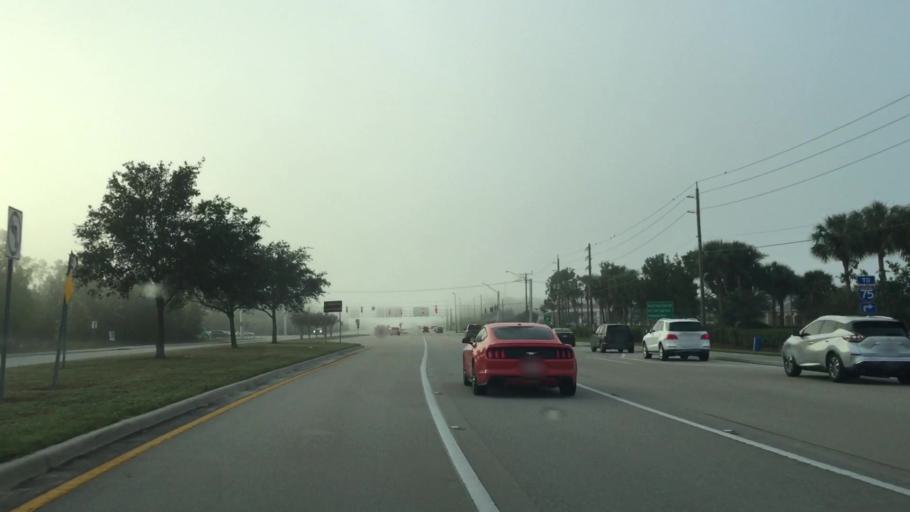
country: US
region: Florida
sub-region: Lee County
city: Gateway
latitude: 26.5494
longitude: -81.7865
